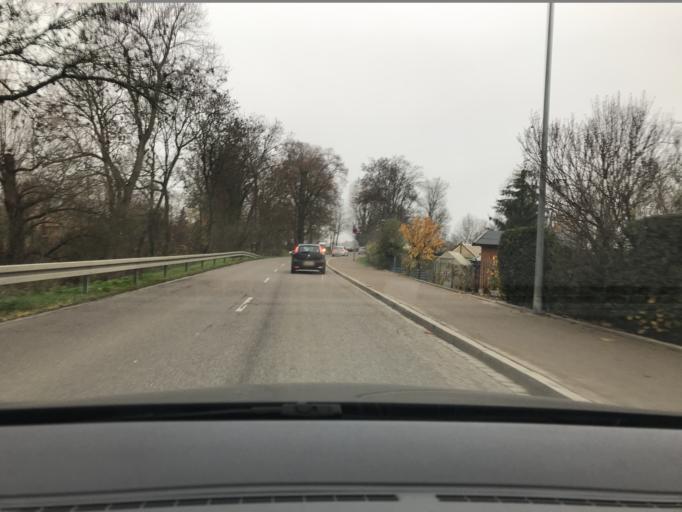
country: DE
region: Bavaria
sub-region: Swabia
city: Noerdlingen
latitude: 48.8495
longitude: 10.4786
